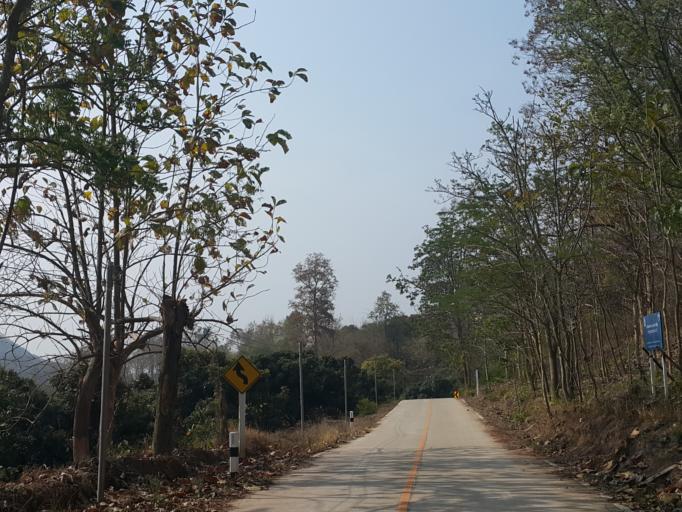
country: TH
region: Chiang Mai
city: Hang Dong
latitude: 18.7381
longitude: 98.8613
